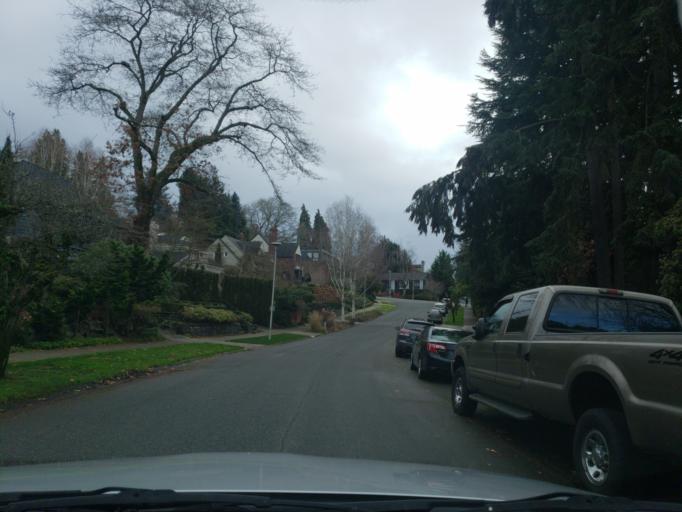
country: US
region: Washington
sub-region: King County
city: Medina
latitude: 47.6533
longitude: -122.2801
